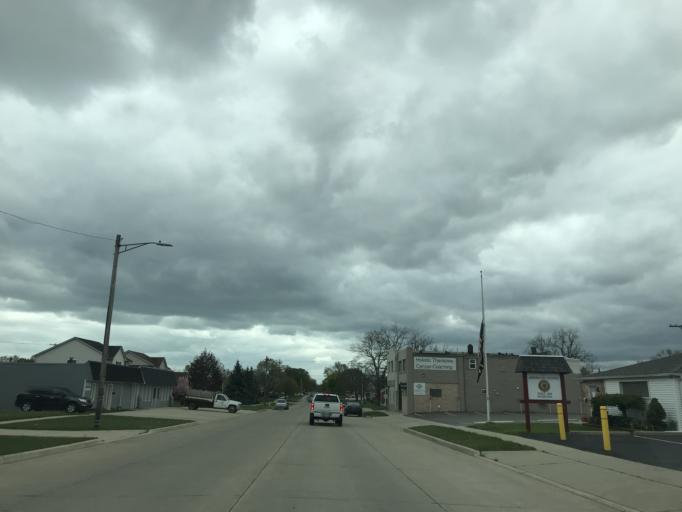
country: US
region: Michigan
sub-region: Wayne County
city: Riverview
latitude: 42.1837
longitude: -83.1796
